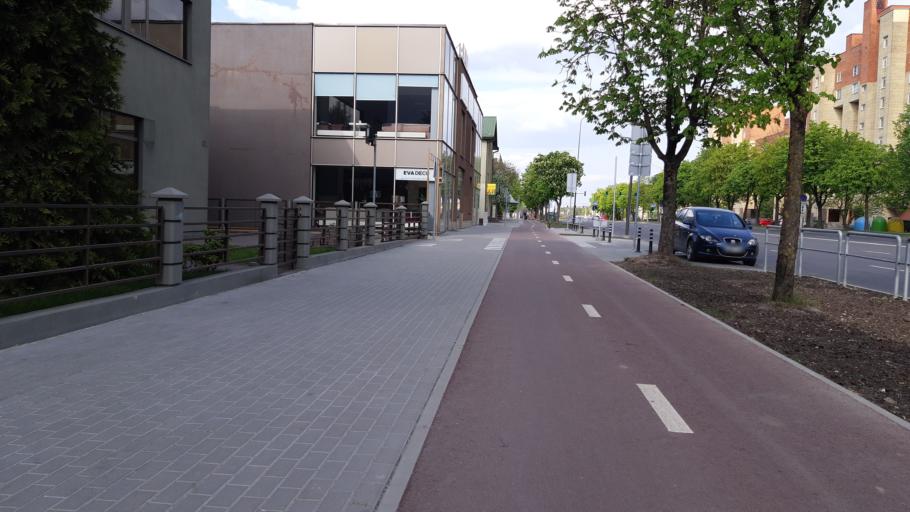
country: LT
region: Kauno apskritis
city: Dainava (Kaunas)
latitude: 54.9260
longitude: 23.9667
